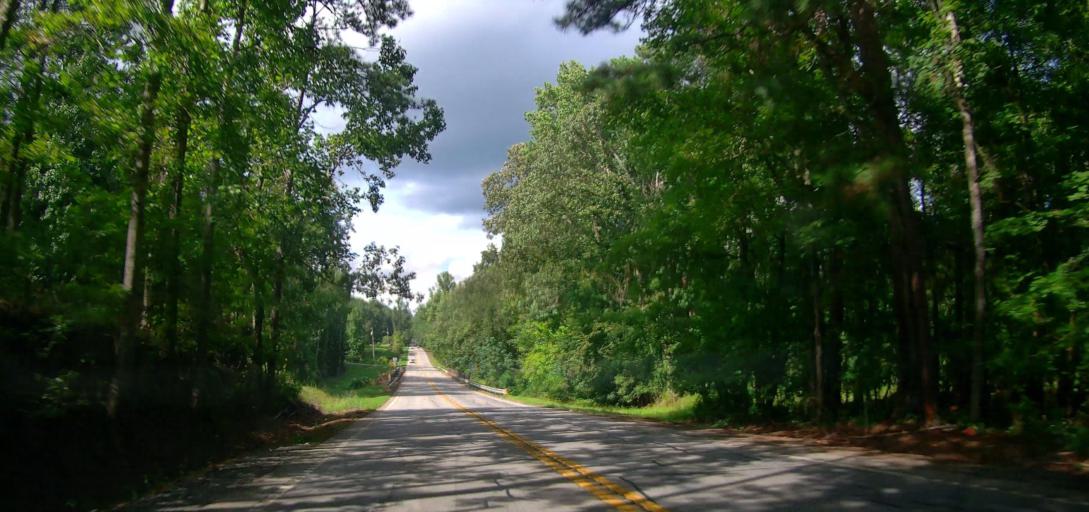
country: US
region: Georgia
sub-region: Harris County
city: Hamilton
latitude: 32.6877
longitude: -84.8570
